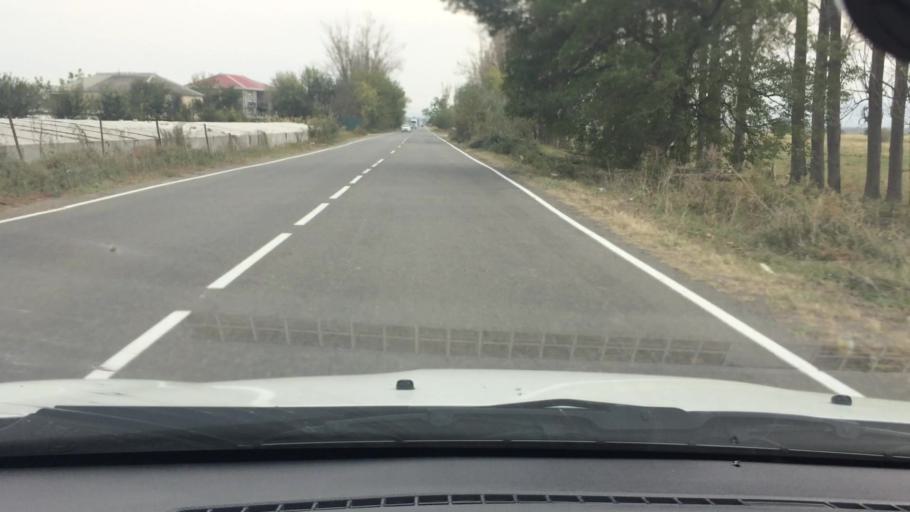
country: GE
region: Kvemo Kartli
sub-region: Gardabani
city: Gardabani
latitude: 41.4467
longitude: 44.9963
